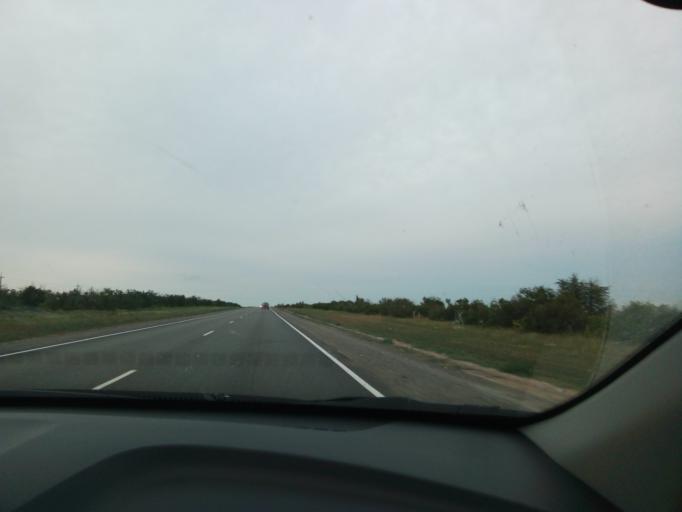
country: RU
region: Volgograd
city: Primorsk
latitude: 49.2022
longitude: 44.8949
